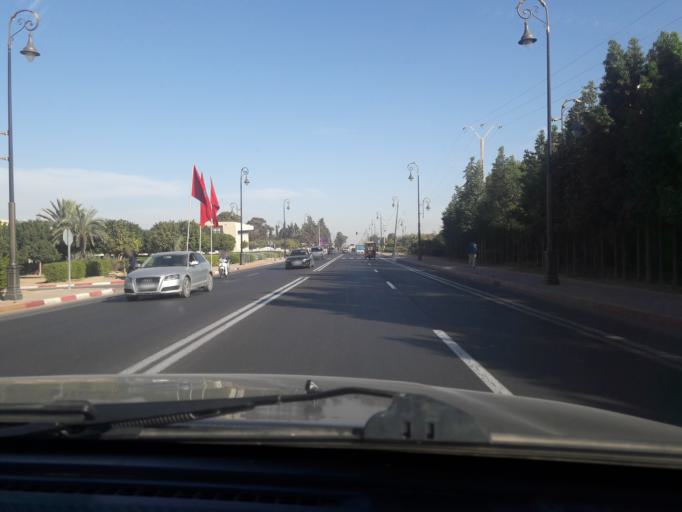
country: MA
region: Marrakech-Tensift-Al Haouz
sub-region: Marrakech
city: Marrakesh
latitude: 31.6482
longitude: -7.9490
